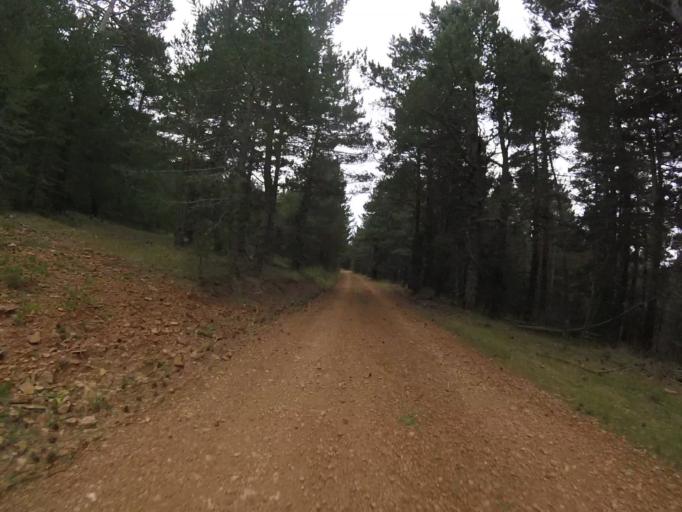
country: ES
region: Aragon
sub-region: Provincia de Teruel
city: Valdelinares
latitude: 40.3665
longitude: -0.6183
